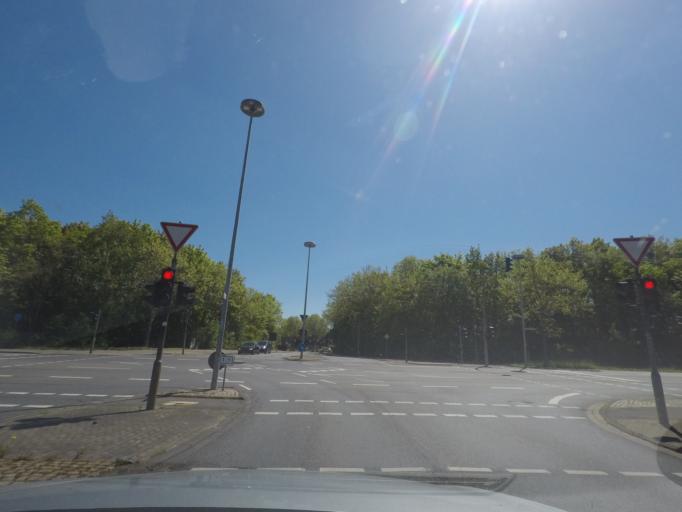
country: DE
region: Lower Saxony
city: Goslar
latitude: 51.9258
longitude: 10.4536
